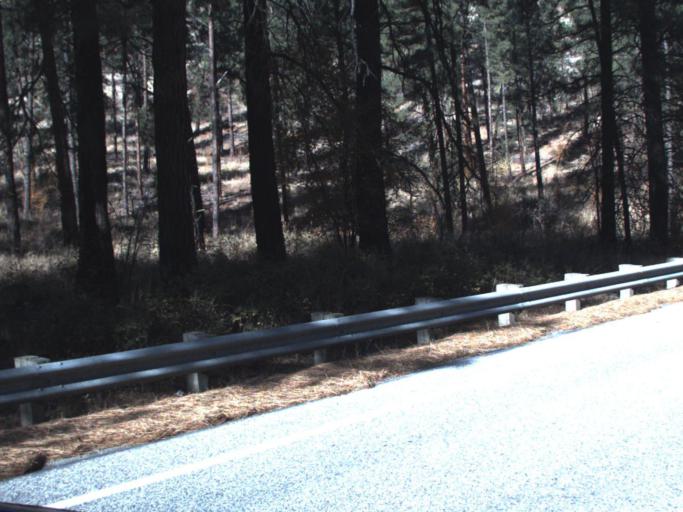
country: US
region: Washington
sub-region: Stevens County
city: Kettle Falls
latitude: 48.5931
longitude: -118.1470
